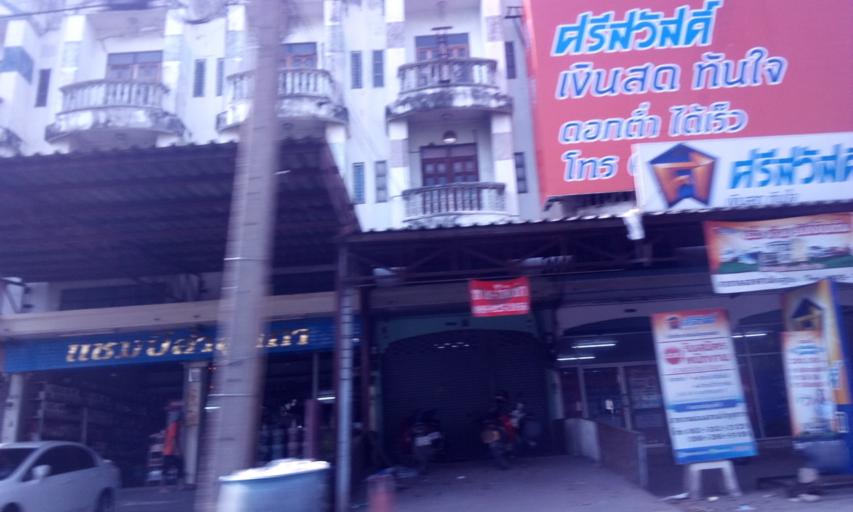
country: TH
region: Bangkok
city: Sai Mai
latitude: 13.9321
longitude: 100.6702
